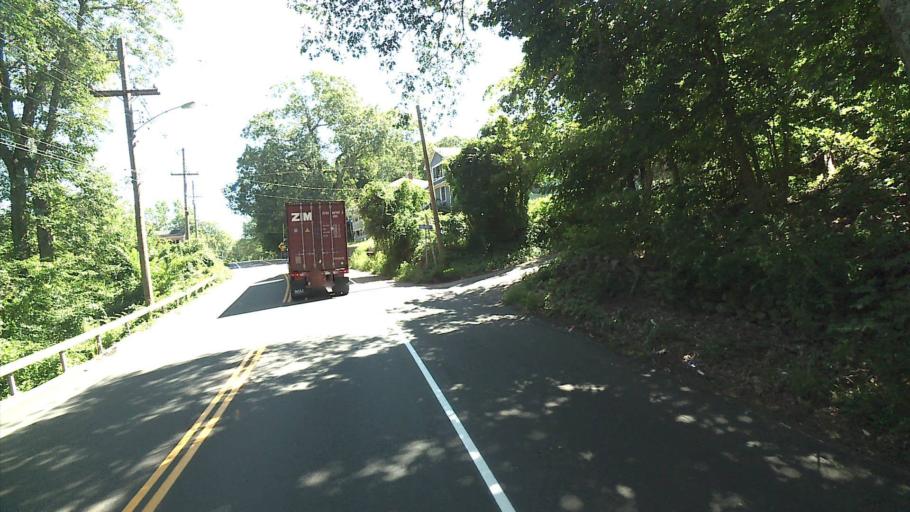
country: US
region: Connecticut
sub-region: New London County
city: Lisbon
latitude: 41.5803
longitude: -72.0459
